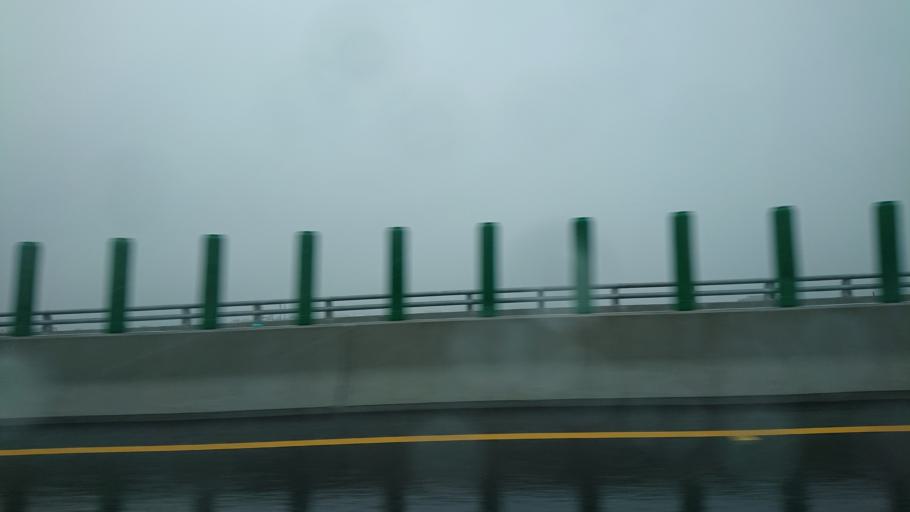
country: TW
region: Taiwan
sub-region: Changhua
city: Chang-hua
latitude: 23.9197
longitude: 120.3117
